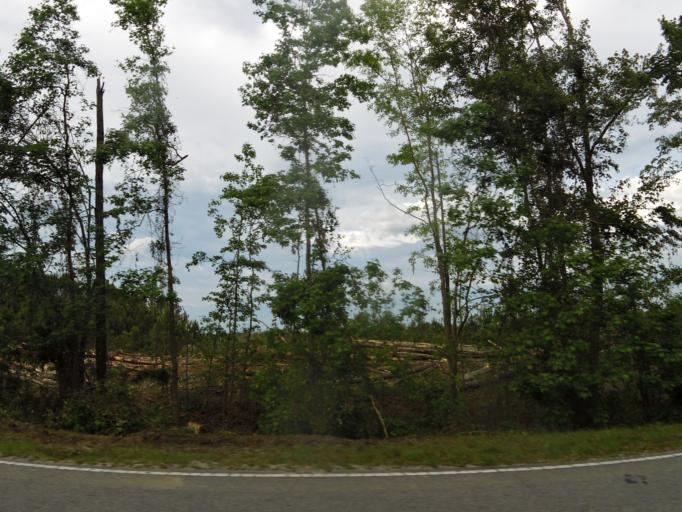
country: US
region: South Carolina
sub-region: Jasper County
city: Hardeeville
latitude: 32.3833
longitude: -81.0972
